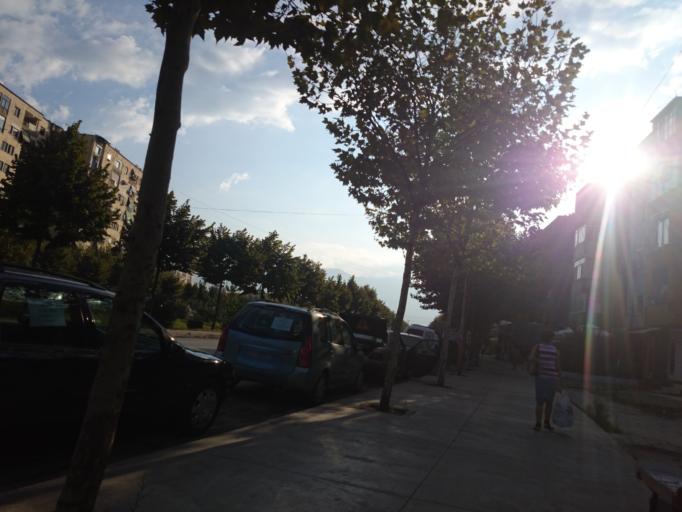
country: AL
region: Tirane
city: Tirana
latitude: 41.3201
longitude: 19.7974
